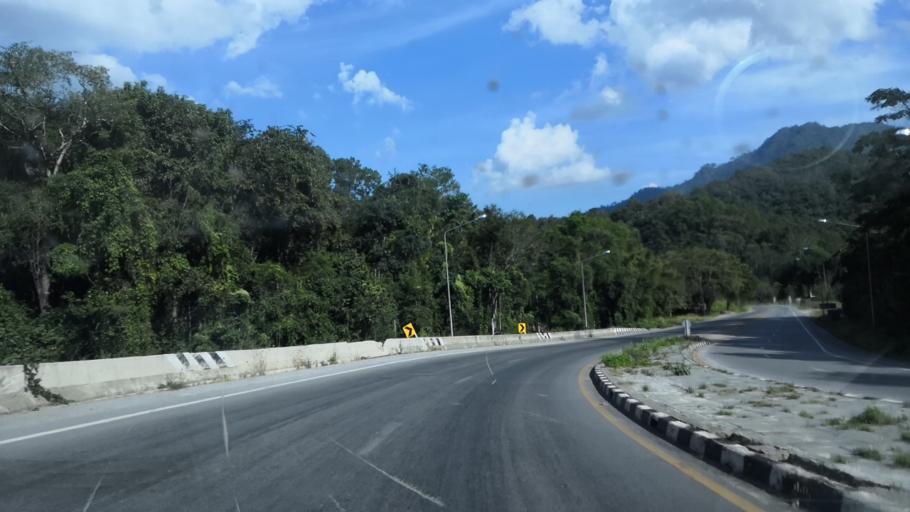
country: TH
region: Lampang
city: Wang Nuea
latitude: 19.0787
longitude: 99.3961
